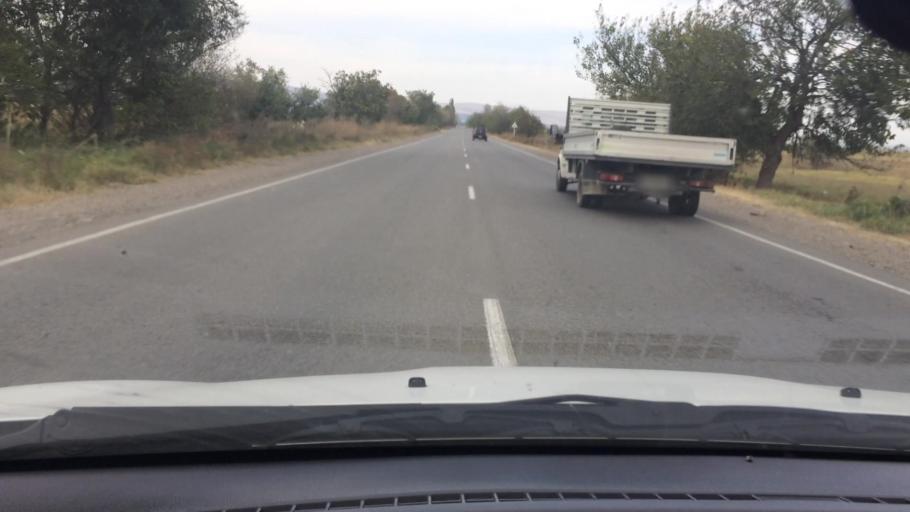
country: GE
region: Kvemo Kartli
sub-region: Marneuli
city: Marneuli
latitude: 41.5467
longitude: 44.7766
